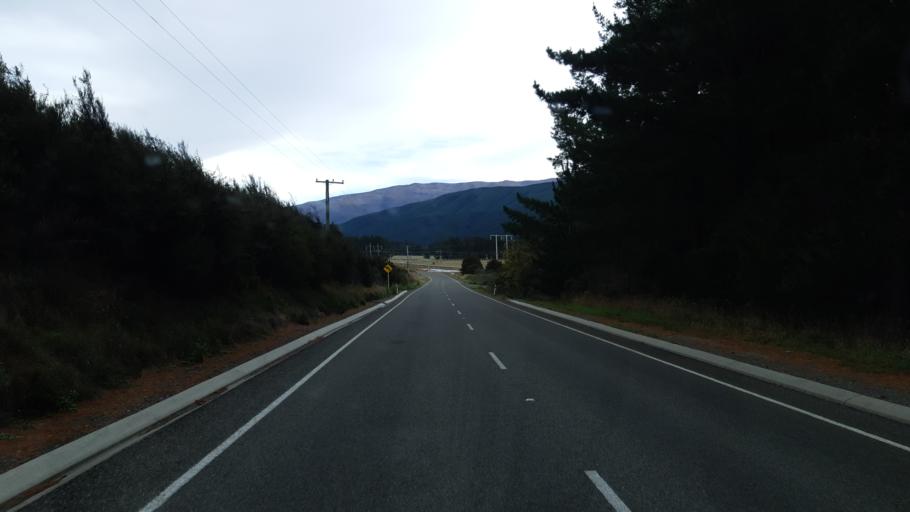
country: NZ
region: Tasman
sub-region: Tasman District
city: Brightwater
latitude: -41.6630
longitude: 173.2148
